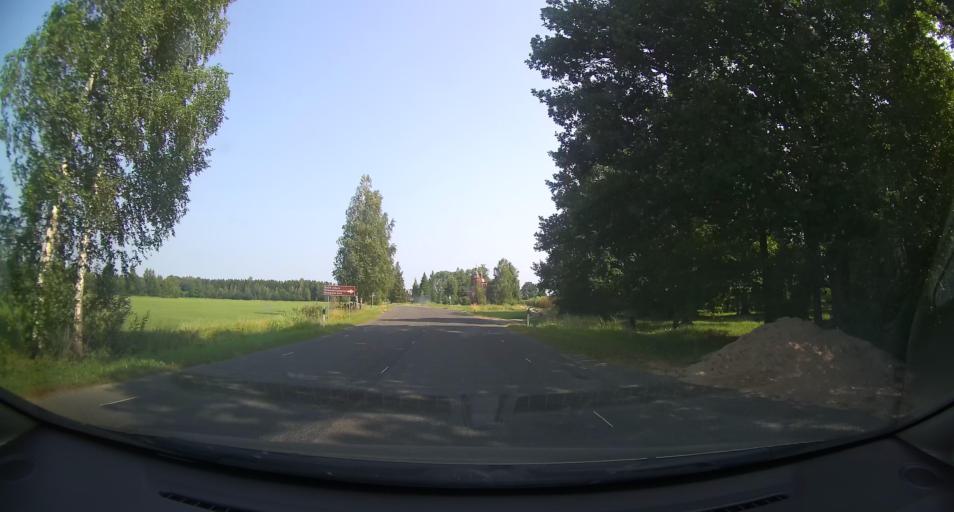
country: EE
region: Paernumaa
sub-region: Audru vald
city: Audru
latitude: 58.4829
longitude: 24.3342
